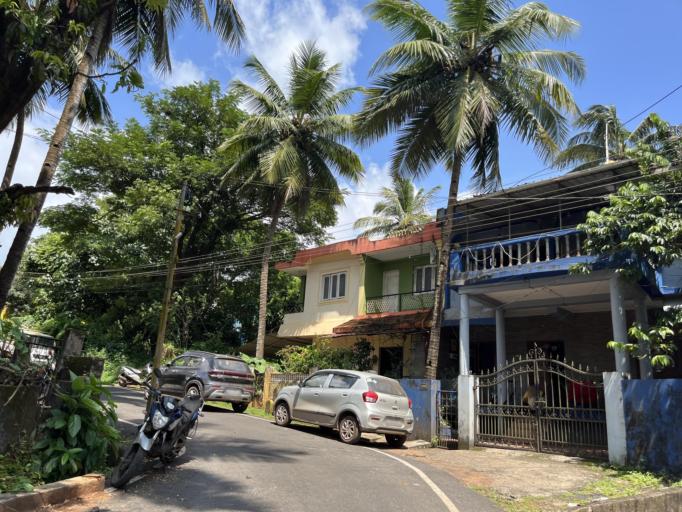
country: IN
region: Goa
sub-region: North Goa
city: Ponda
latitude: 15.3984
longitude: 74.0146
